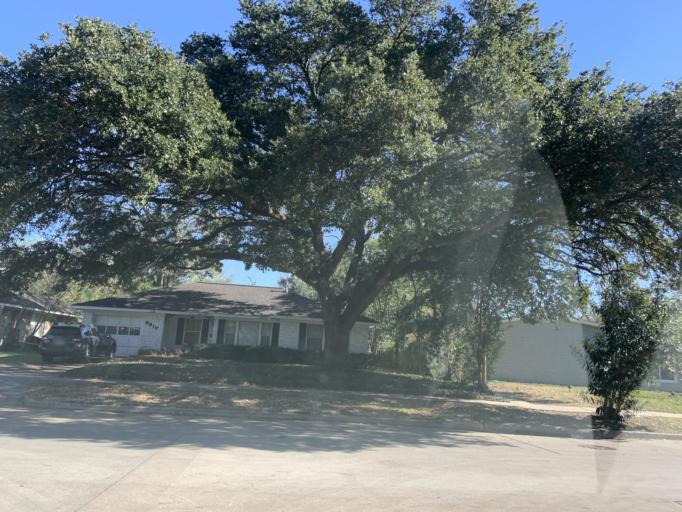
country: US
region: Texas
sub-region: Harris County
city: Bellaire
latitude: 29.6823
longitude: -95.5060
